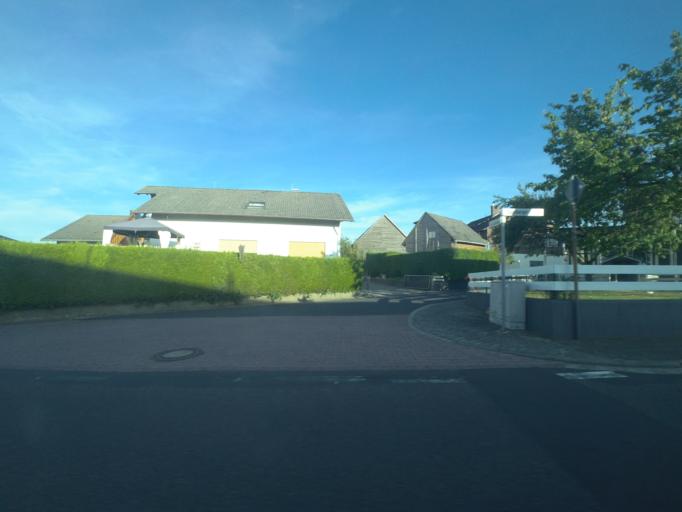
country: DE
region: Hesse
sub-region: Regierungsbezirk Darmstadt
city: Wachtersbach
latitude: 50.2880
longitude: 9.2614
